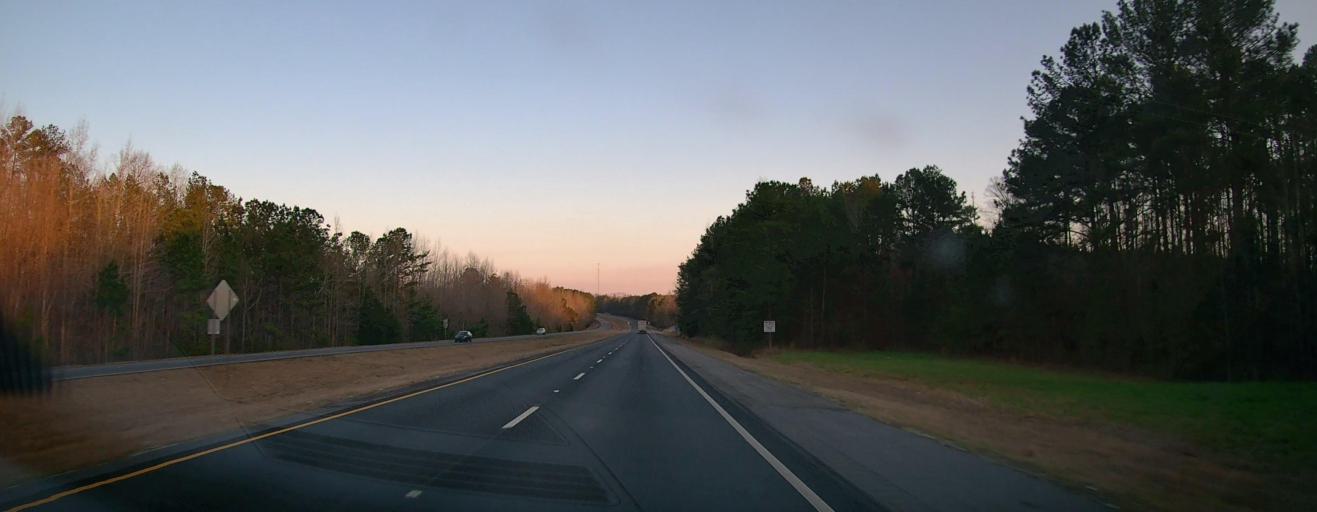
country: US
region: Alabama
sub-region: Coosa County
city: Goodwater
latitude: 33.0541
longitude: -86.1451
